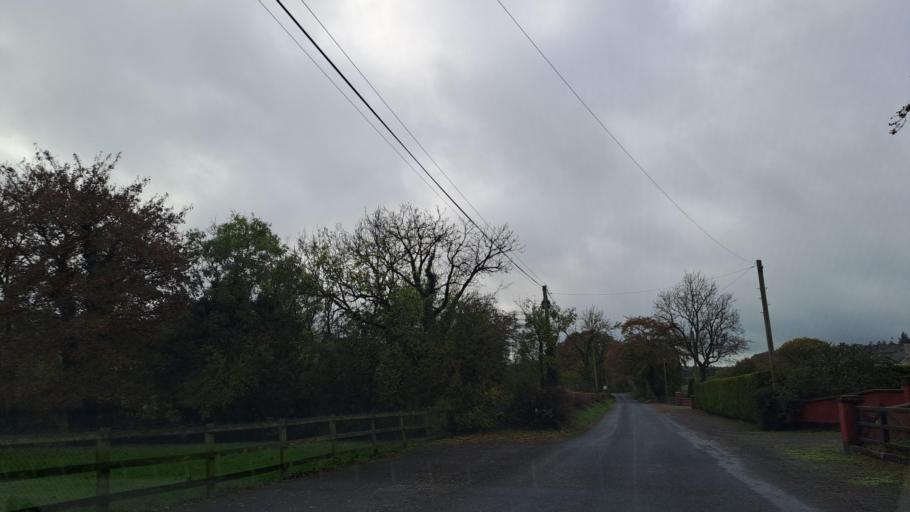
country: IE
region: Ulster
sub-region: An Cabhan
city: Bailieborough
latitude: 53.9351
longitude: -6.9731
